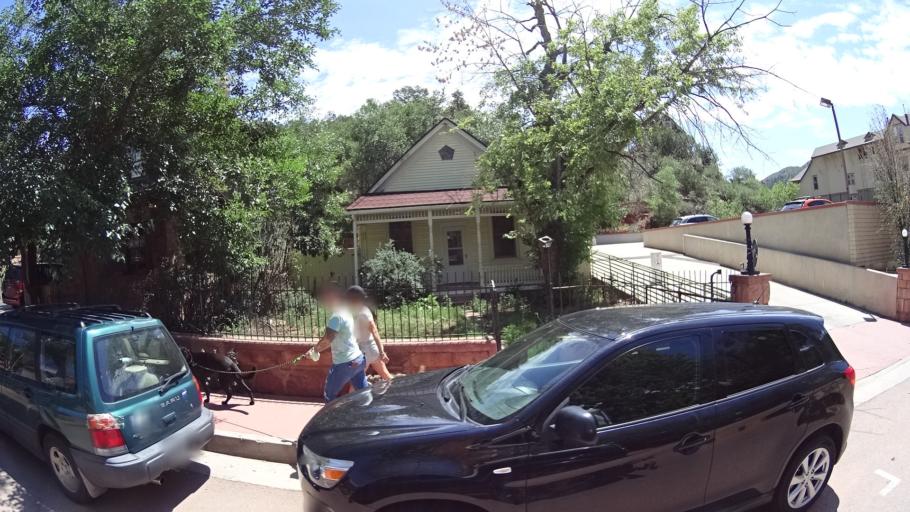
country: US
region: Colorado
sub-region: El Paso County
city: Manitou Springs
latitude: 38.8603
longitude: -104.9176
